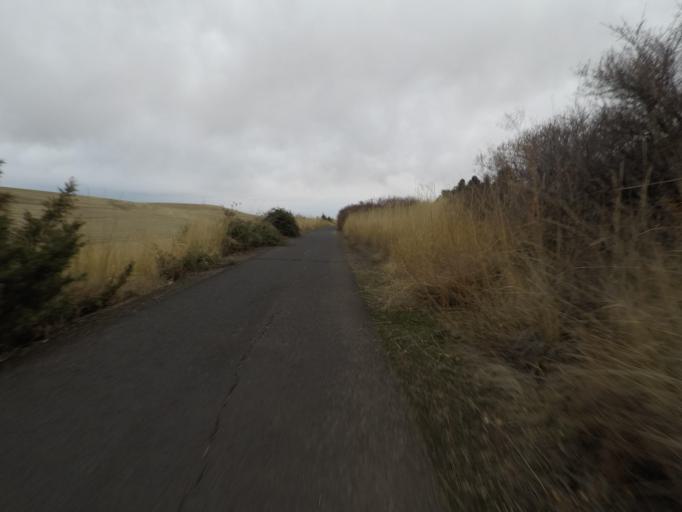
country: US
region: Washington
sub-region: Walla Walla County
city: Walla Walla East
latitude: 46.0651
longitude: -118.2678
